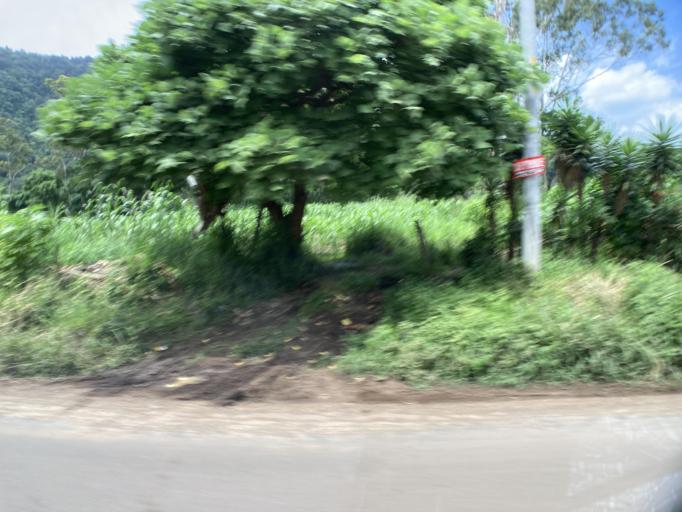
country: GT
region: Guatemala
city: Villa Canales
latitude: 14.4216
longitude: -90.5446
